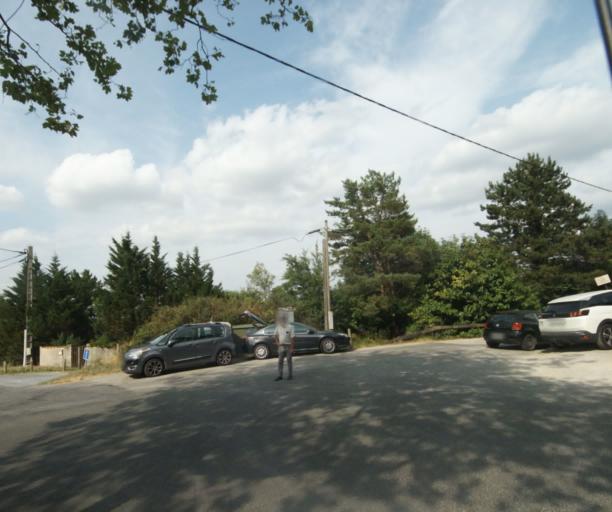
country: FR
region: Midi-Pyrenees
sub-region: Departement de la Haute-Garonne
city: Revel
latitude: 43.4411
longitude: 2.0314
